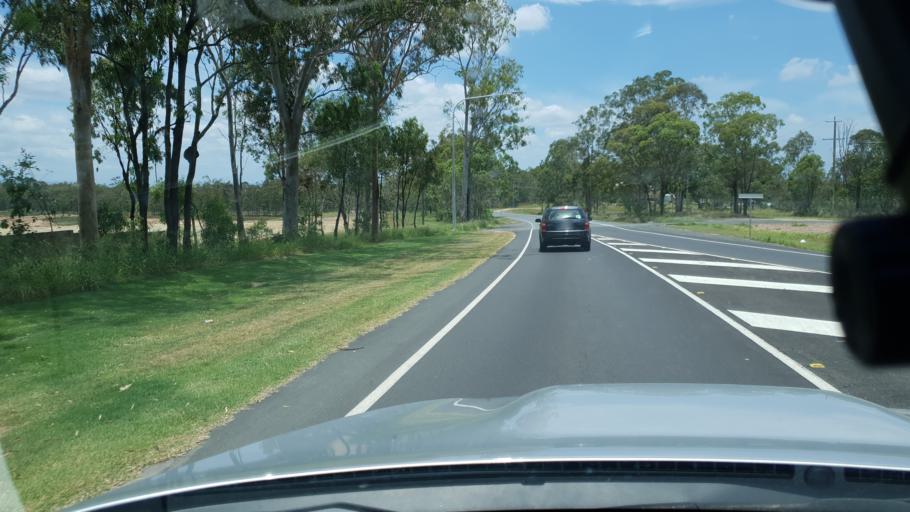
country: AU
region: Queensland
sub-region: Logan
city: North Maclean
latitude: -27.7397
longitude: 152.9846
